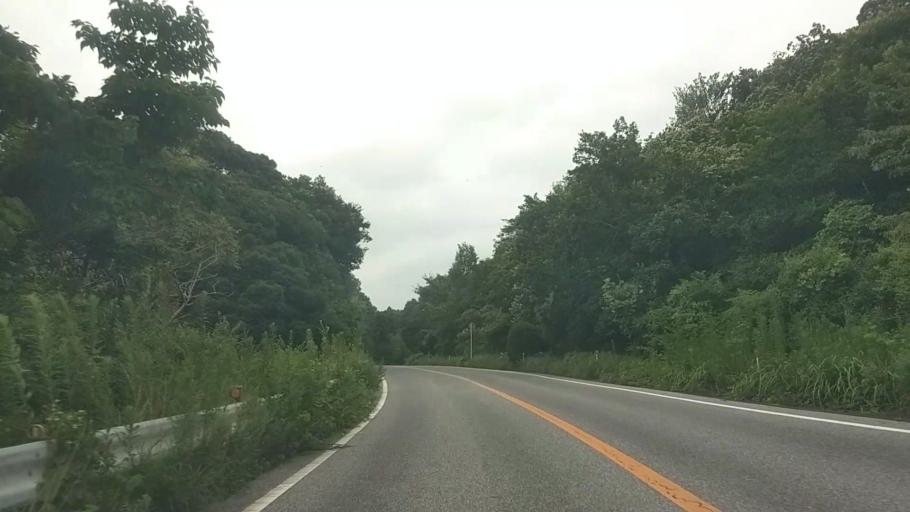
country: JP
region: Chiba
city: Kimitsu
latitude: 35.2406
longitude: 140.0066
